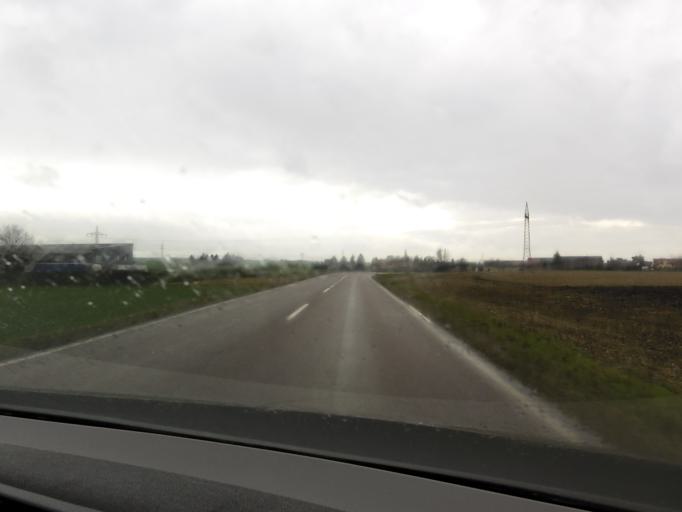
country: DE
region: Saxony-Anhalt
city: Grosskorbetha
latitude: 51.2245
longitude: 12.0378
